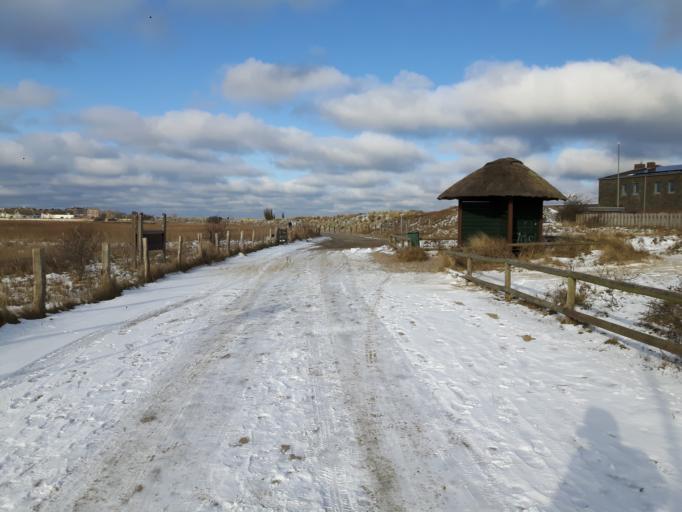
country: DE
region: Schleswig-Holstein
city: Heiligenhafen
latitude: 54.3799
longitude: 10.9912
